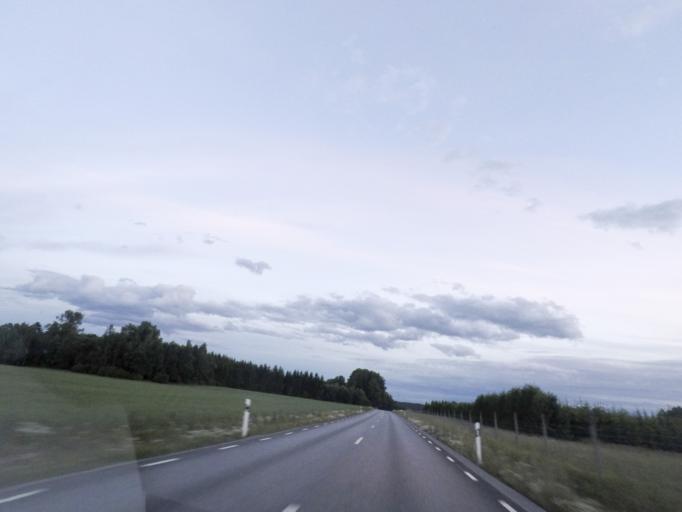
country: SE
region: Uppsala
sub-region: Habo Kommun
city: Balsta
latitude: 59.6389
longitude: 17.5248
